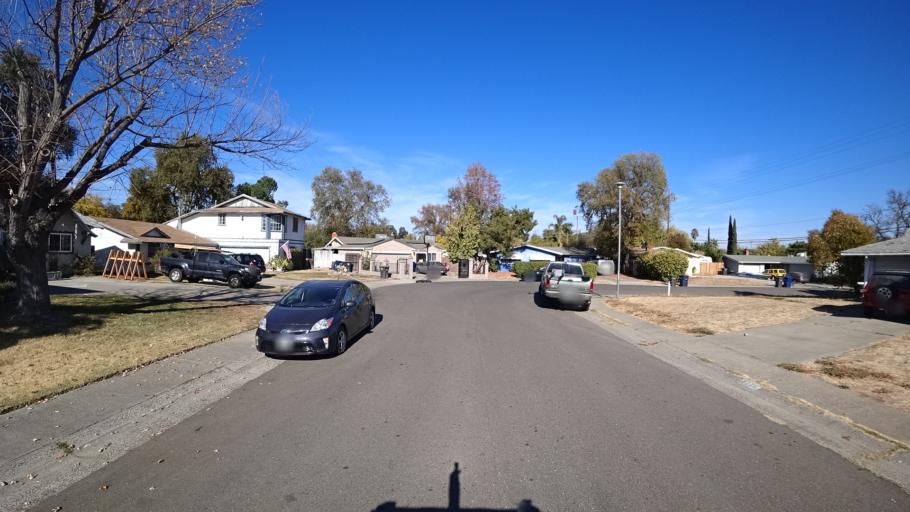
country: US
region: California
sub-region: Sacramento County
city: Antelope
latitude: 38.7164
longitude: -121.3093
